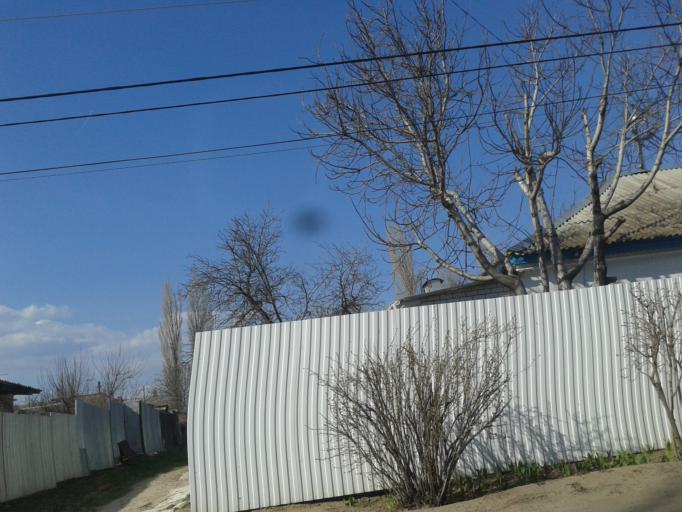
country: RU
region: Volgograd
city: Volgograd
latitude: 48.6305
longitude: 44.3912
